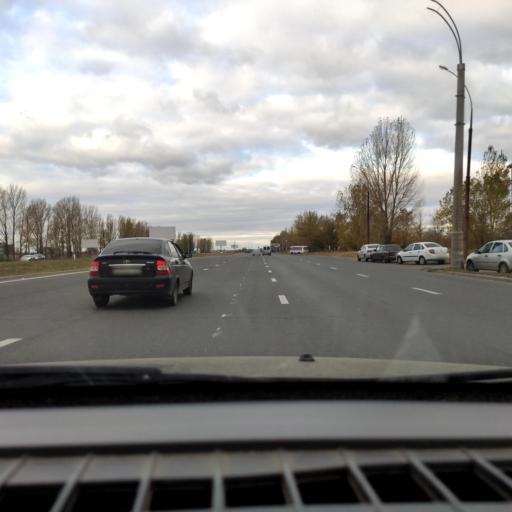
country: RU
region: Samara
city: Podstepki
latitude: 53.5588
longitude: 49.2248
